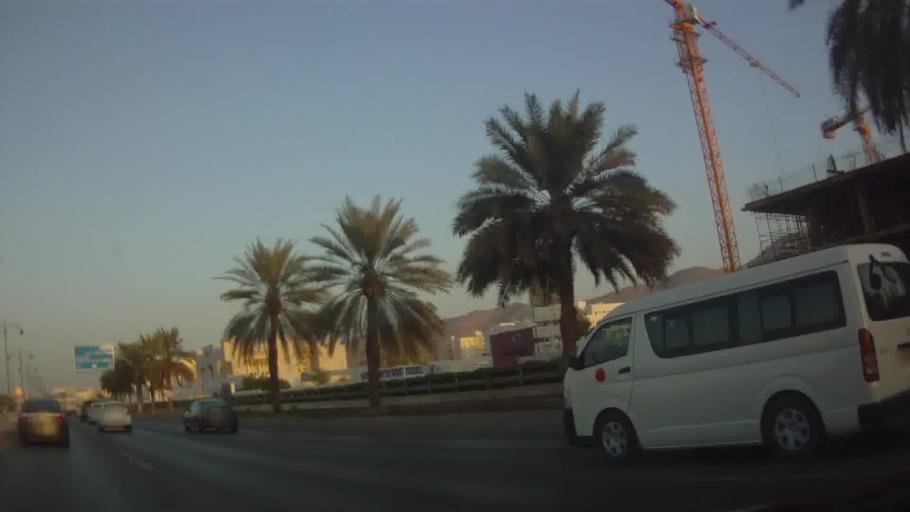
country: OM
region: Muhafazat Masqat
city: Bawshar
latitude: 23.5971
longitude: 58.4338
